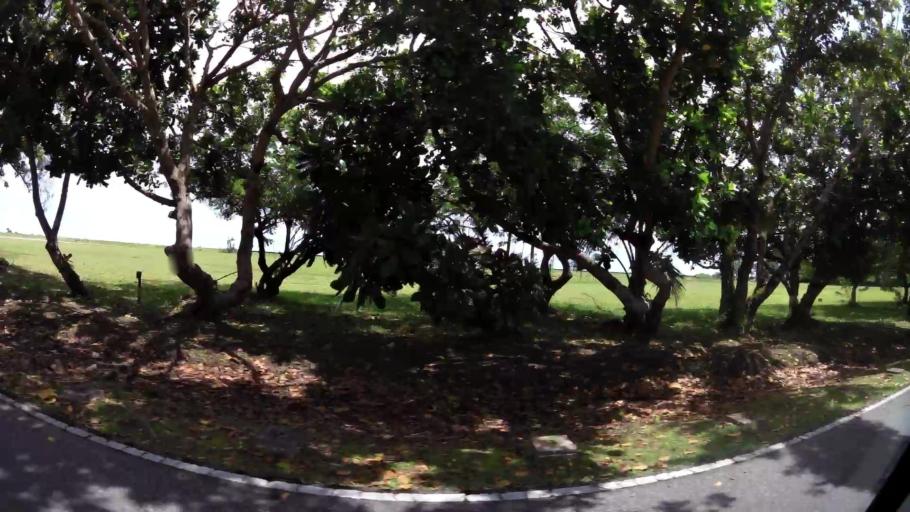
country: BN
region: Belait
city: Seria
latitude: 4.6073
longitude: 114.2928
